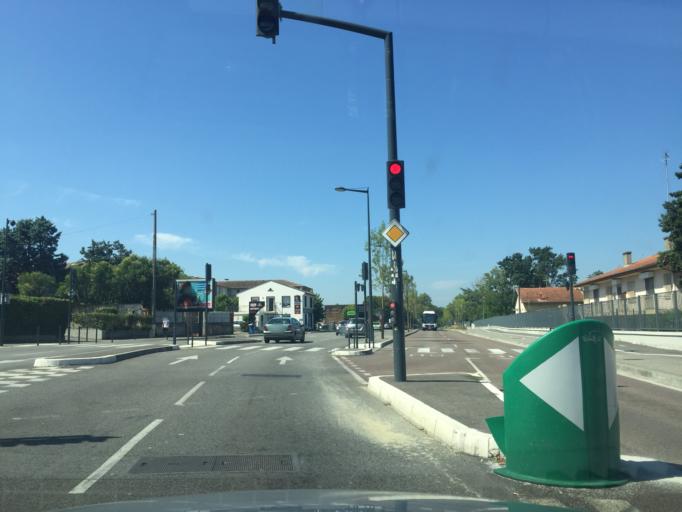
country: FR
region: Midi-Pyrenees
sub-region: Departement de la Haute-Garonne
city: Ramonville-Saint-Agne
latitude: 43.5558
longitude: 1.4663
